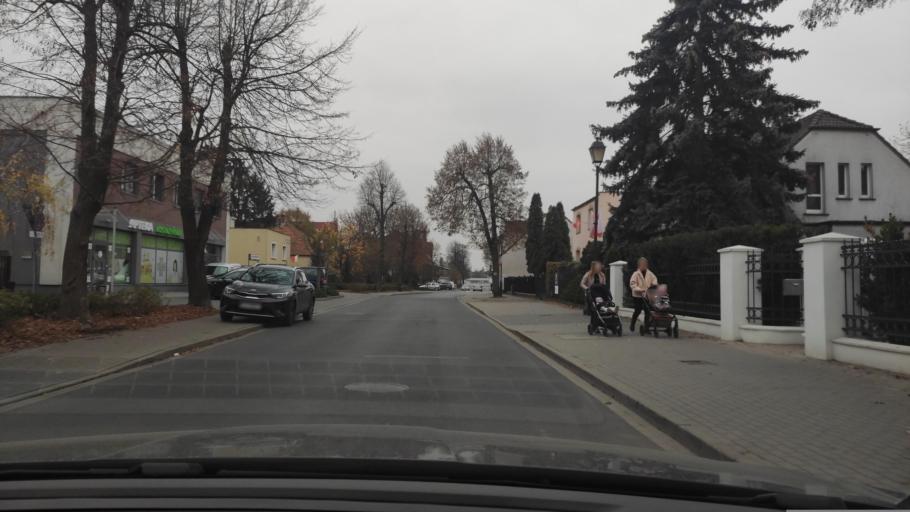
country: PL
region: Greater Poland Voivodeship
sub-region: Powiat poznanski
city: Kostrzyn
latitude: 52.3961
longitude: 17.2264
